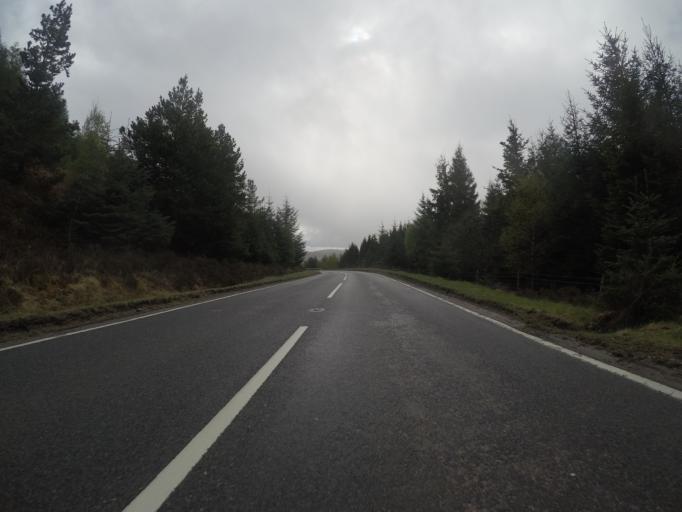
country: GB
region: Scotland
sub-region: Highland
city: Spean Bridge
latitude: 57.0827
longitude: -4.9560
